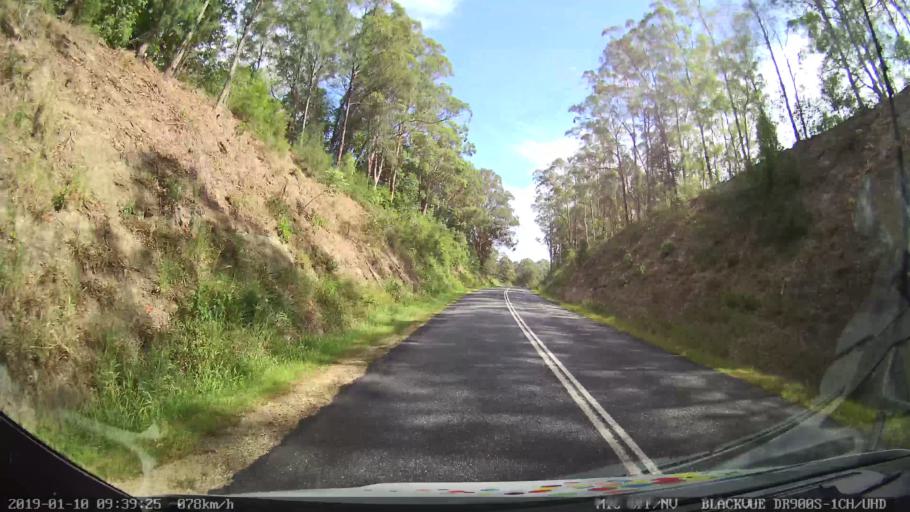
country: AU
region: New South Wales
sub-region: Coffs Harbour
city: Nana Glen
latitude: -30.1636
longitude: 153.0025
